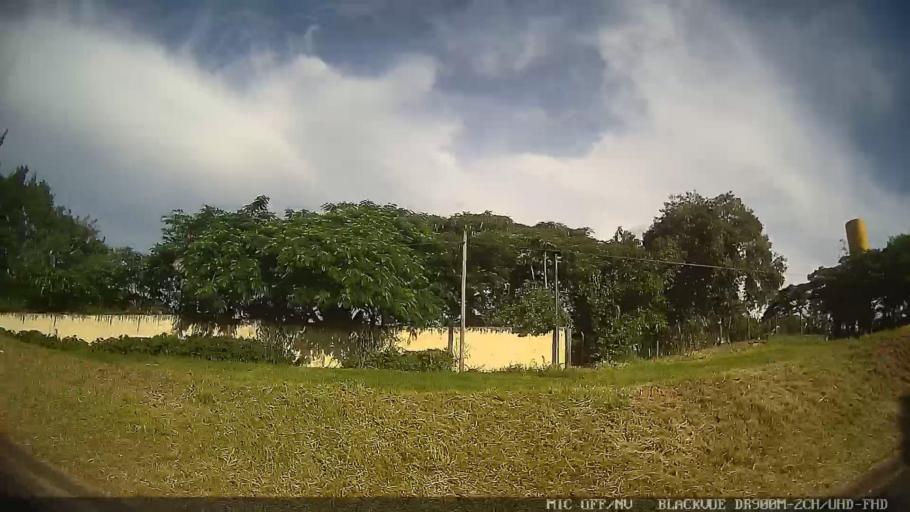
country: BR
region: Sao Paulo
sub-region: Tiete
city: Tiete
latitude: -23.1130
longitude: -47.6972
